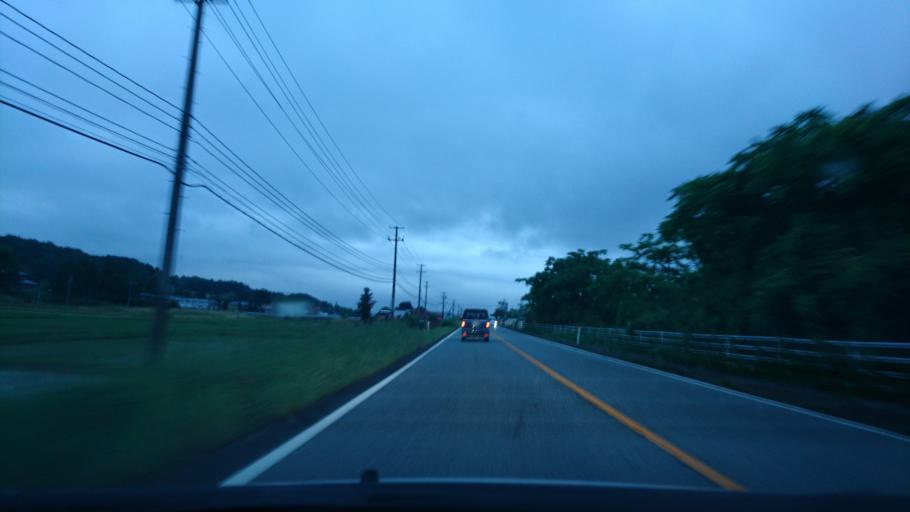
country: JP
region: Iwate
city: Ichinoseki
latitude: 38.8282
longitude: 141.0814
